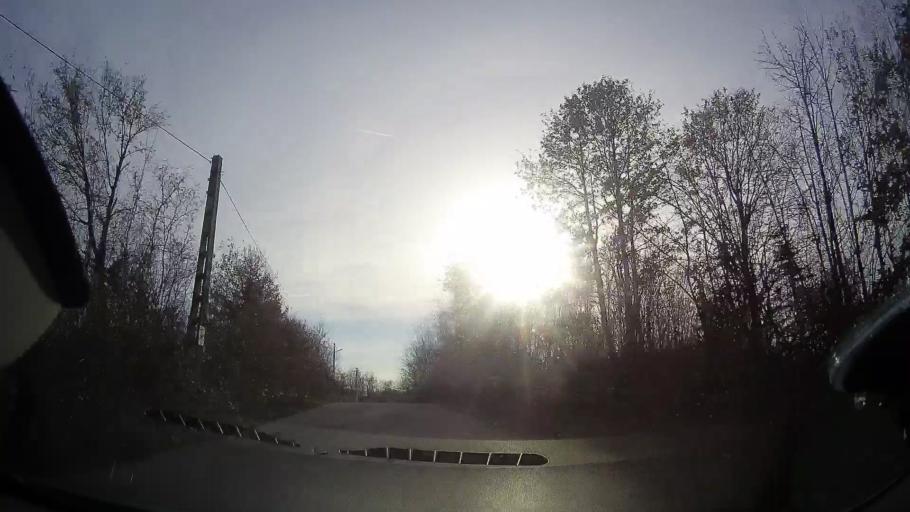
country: RO
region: Bihor
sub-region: Comuna Sarbi
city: Burzuc
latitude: 47.1134
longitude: 22.1789
